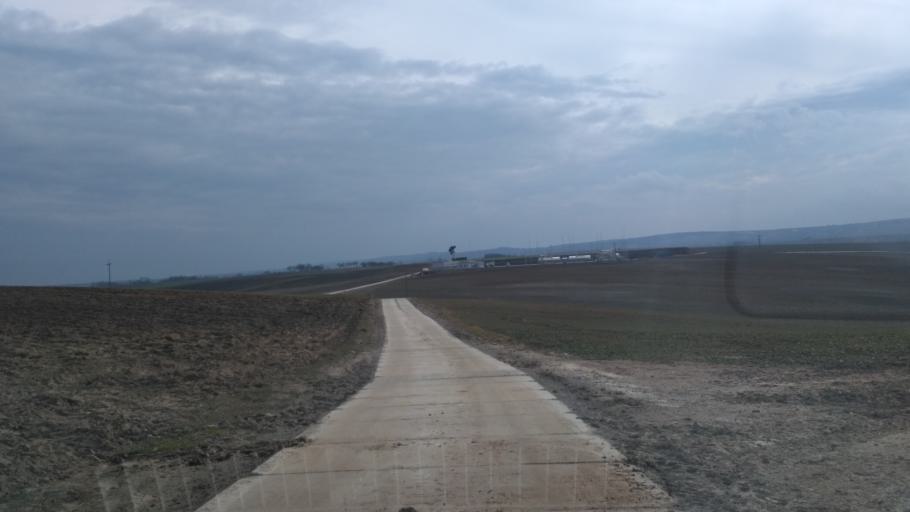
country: PL
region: Subcarpathian Voivodeship
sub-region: Powiat jaroslawski
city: Rokietnica
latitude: 49.9291
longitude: 22.5931
